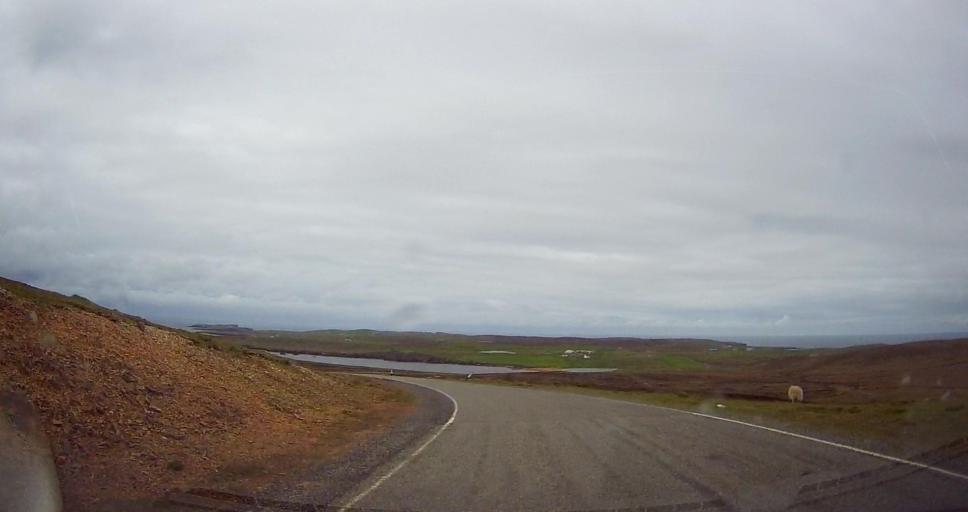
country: GB
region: Scotland
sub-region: Shetland Islands
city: Lerwick
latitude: 60.4879
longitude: -1.5282
